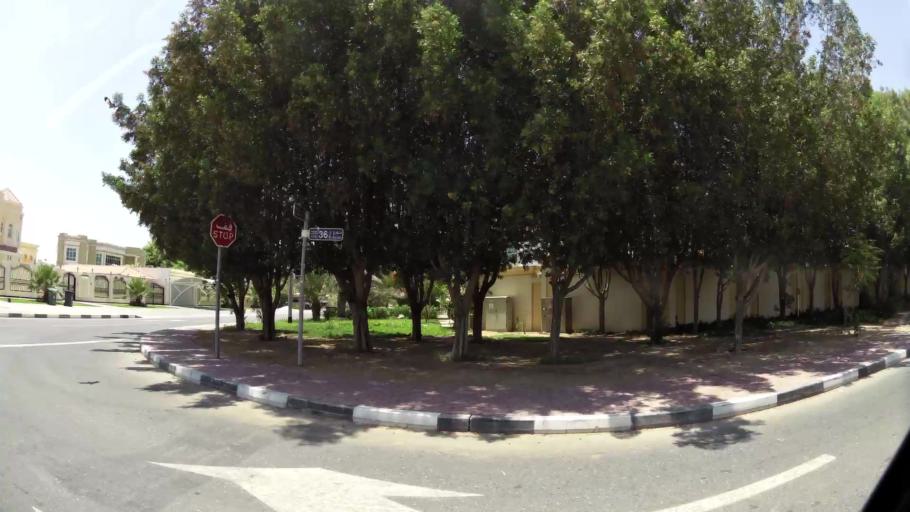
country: AE
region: Dubai
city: Dubai
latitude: 25.0917
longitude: 55.2009
